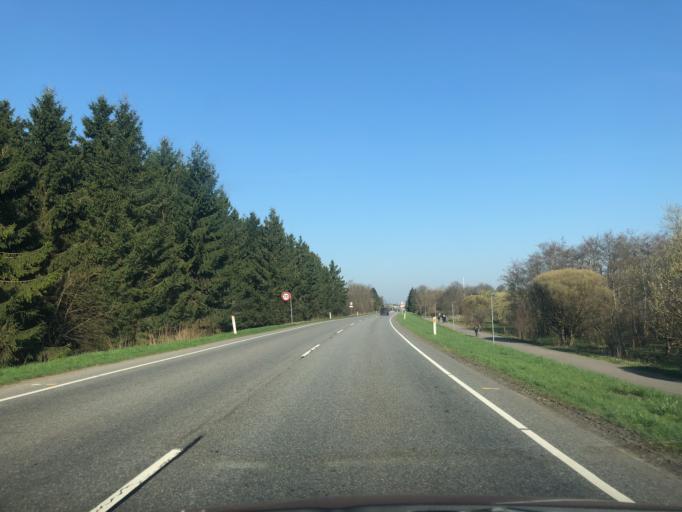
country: DK
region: Zealand
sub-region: Faxe Kommune
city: Haslev
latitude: 55.3174
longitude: 11.9513
